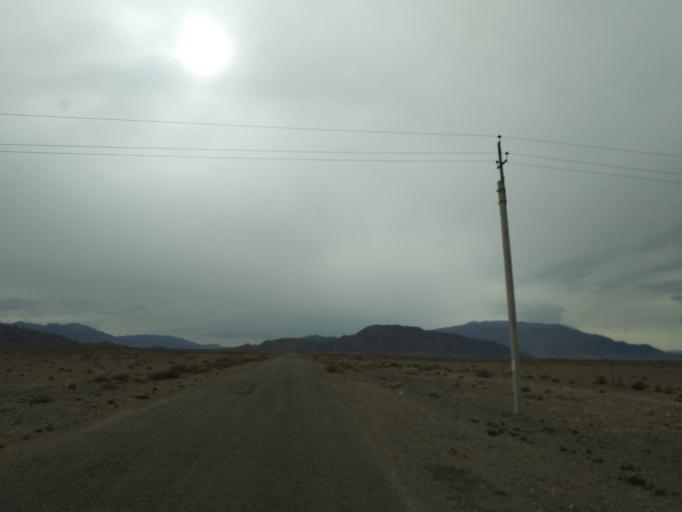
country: KG
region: Ysyk-Koel
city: Balykchy
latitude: 42.3209
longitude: 76.2142
